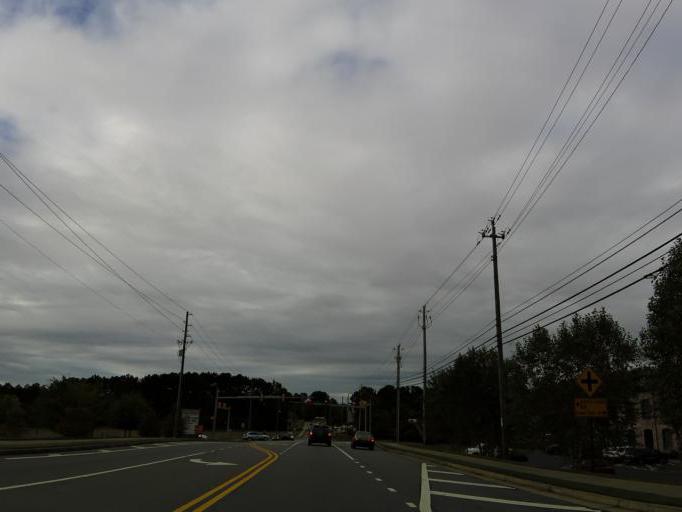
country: US
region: Georgia
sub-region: Cobb County
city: Acworth
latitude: 34.0377
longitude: -84.6750
